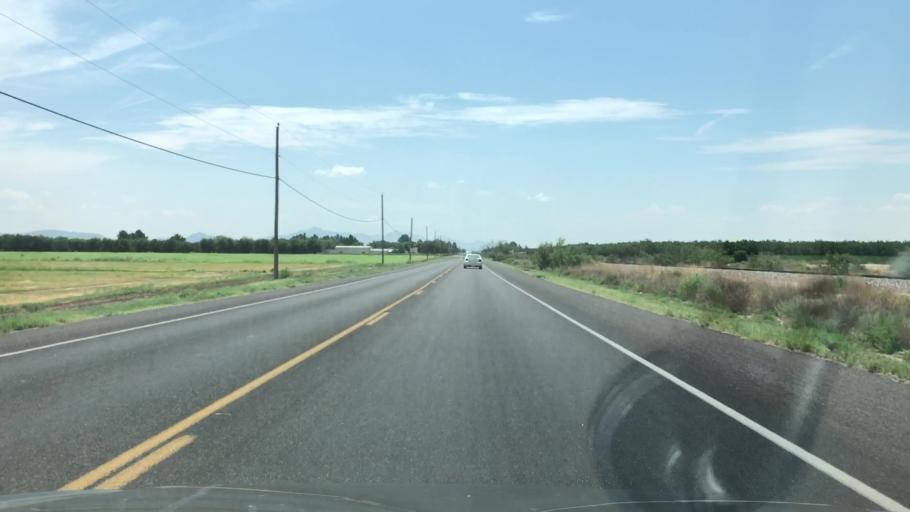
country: US
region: New Mexico
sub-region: Dona Ana County
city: Mesquite
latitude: 32.1866
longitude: -106.7105
